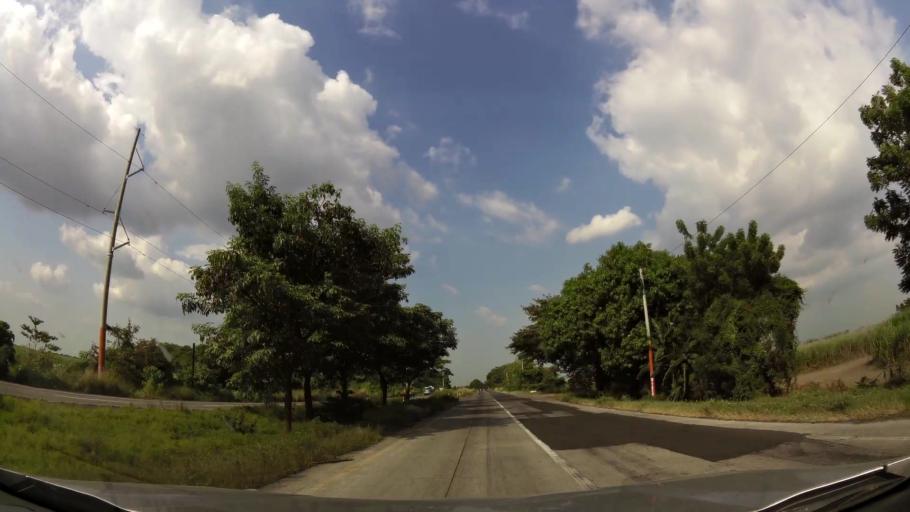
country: GT
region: Escuintla
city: Puerto San Jose
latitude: 14.0413
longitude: -90.7786
